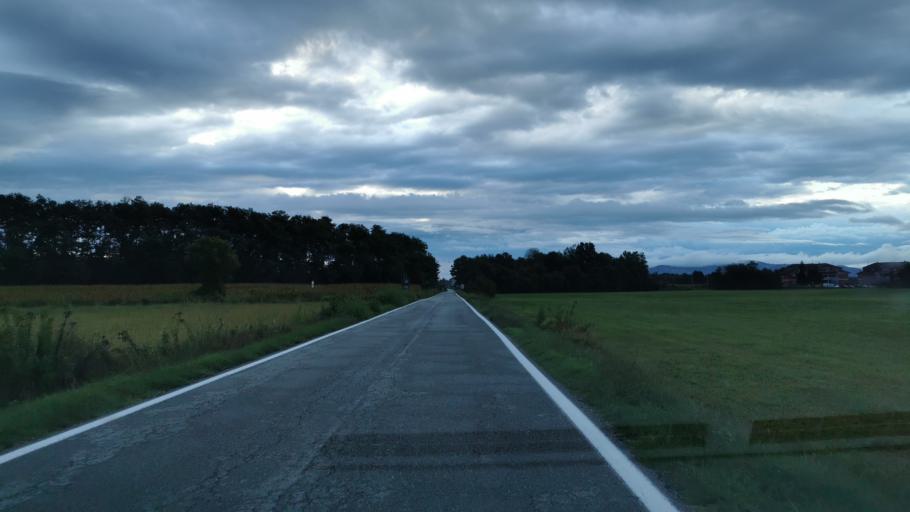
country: IT
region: Piedmont
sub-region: Provincia di Torino
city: San Benigno Canavese
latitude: 45.2225
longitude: 7.7696
